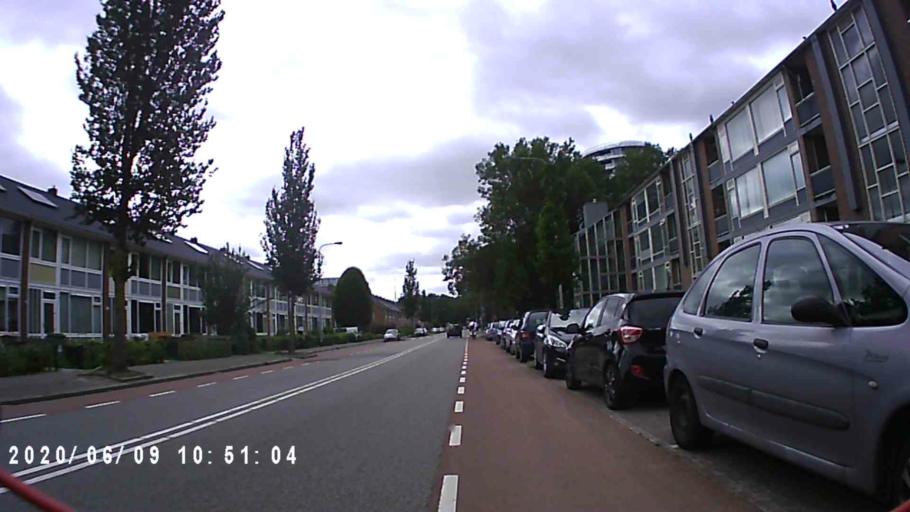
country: NL
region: Groningen
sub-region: Gemeente Groningen
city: Korrewegwijk
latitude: 53.2363
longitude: 6.5550
